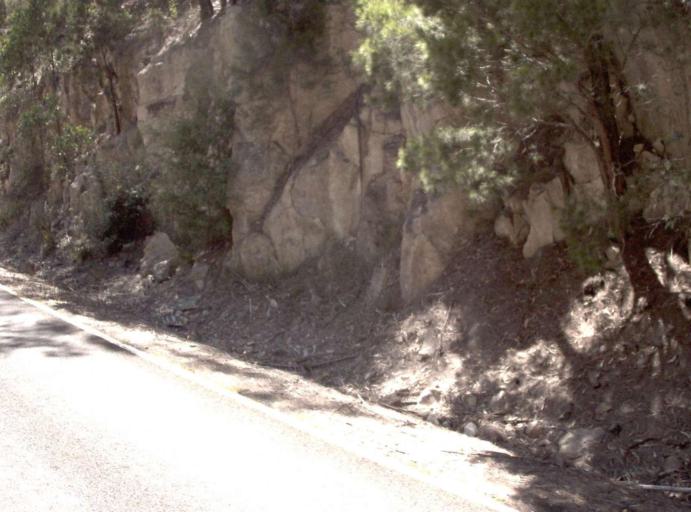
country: AU
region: Victoria
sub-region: East Gippsland
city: Lakes Entrance
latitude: -37.3743
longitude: 148.2181
